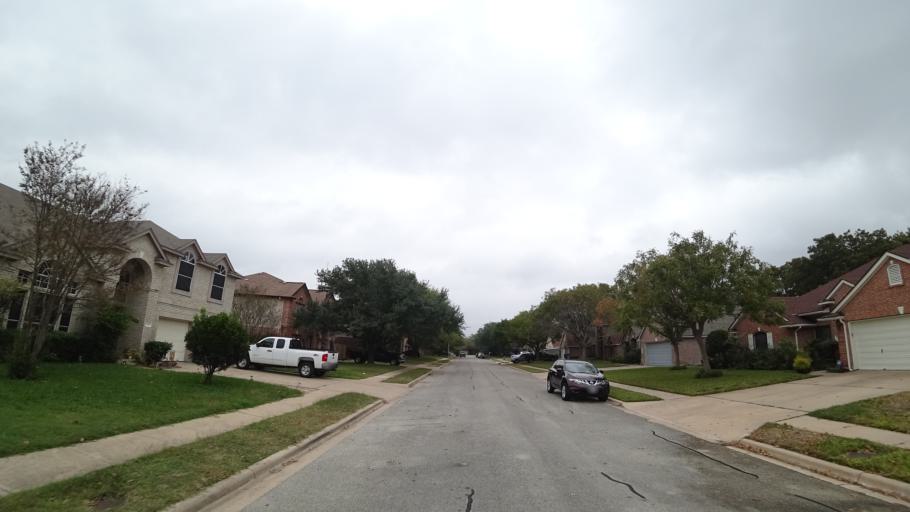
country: US
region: Texas
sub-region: Travis County
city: Pflugerville
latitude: 30.4501
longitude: -97.6145
